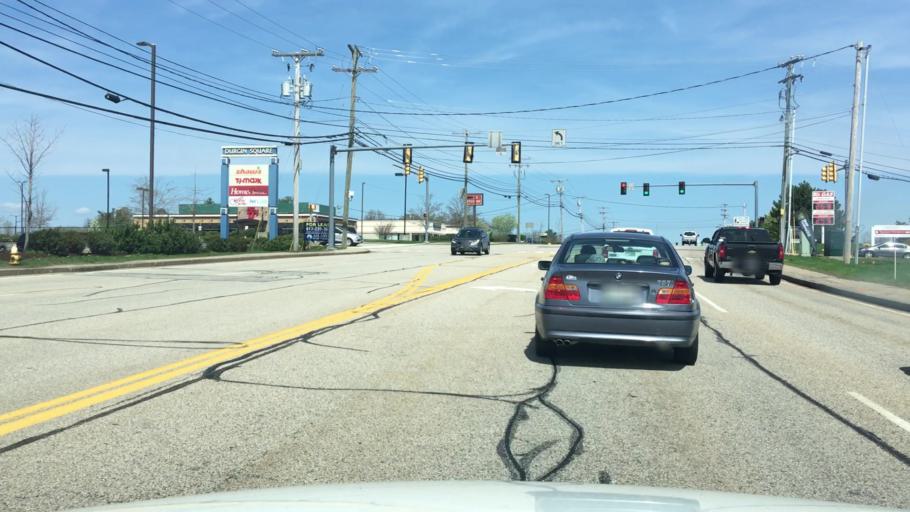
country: US
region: Maine
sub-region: York County
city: South Eliot
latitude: 43.0883
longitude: -70.7902
